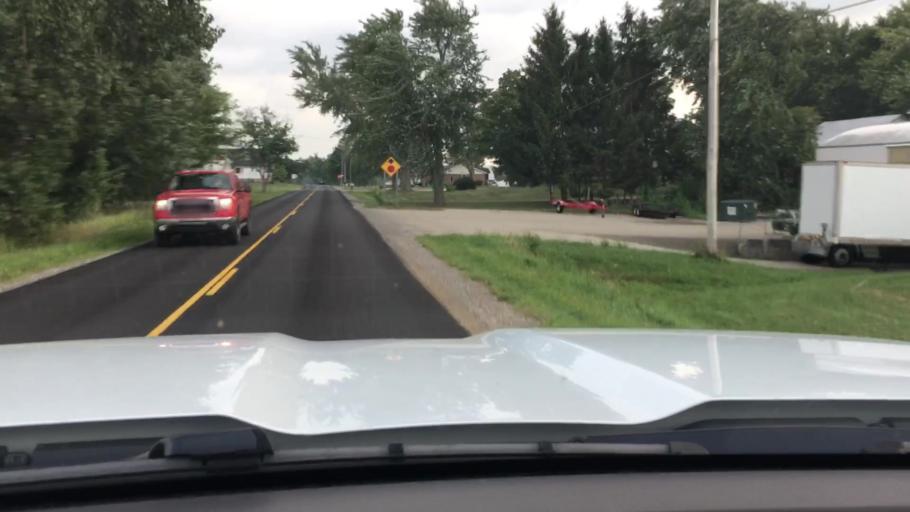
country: US
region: Michigan
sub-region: Ottawa County
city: Hudsonville
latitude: 42.8281
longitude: -85.8817
